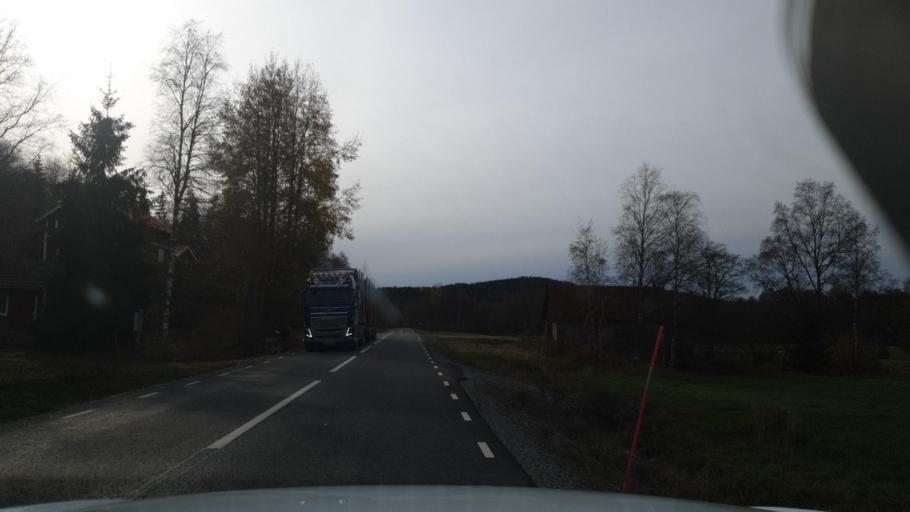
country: SE
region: Vaermland
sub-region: Arjangs Kommun
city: Arjaeng
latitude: 59.5843
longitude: 12.1255
